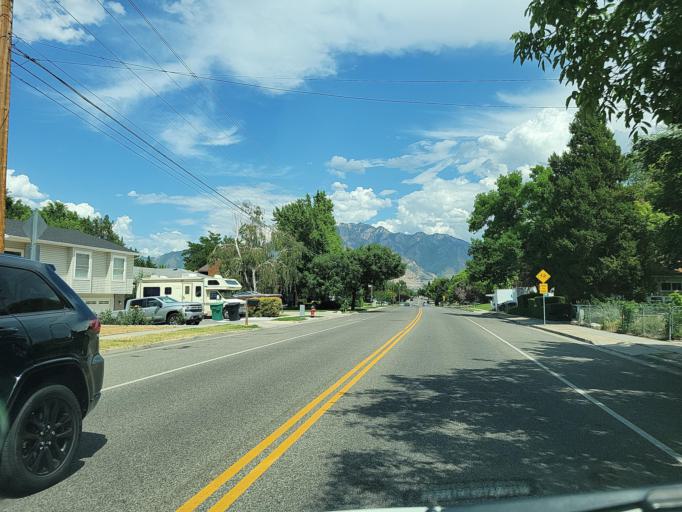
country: US
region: Utah
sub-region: Salt Lake County
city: Murray
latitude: 40.6417
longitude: -111.8779
